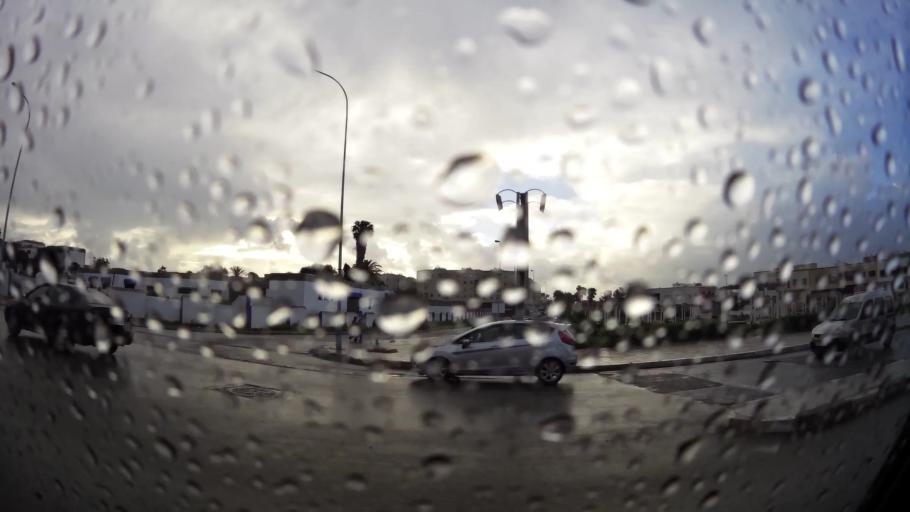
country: MA
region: Doukkala-Abda
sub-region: El-Jadida
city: El Jadida
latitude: 33.2392
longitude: -8.5170
